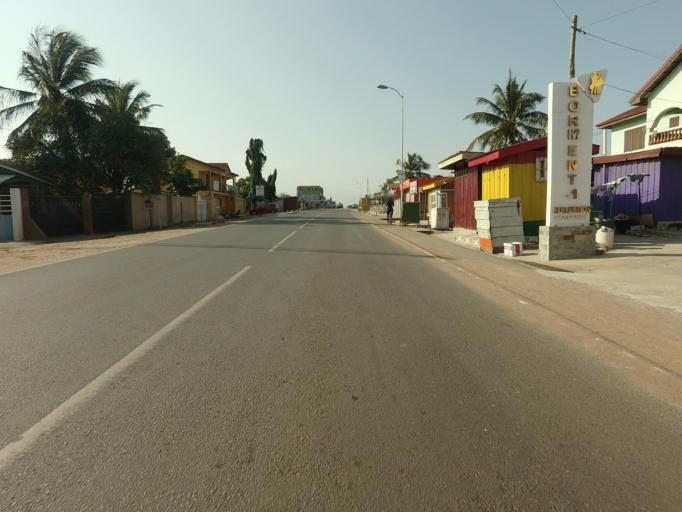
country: GH
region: Greater Accra
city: Nungua
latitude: 5.6293
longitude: -0.0763
